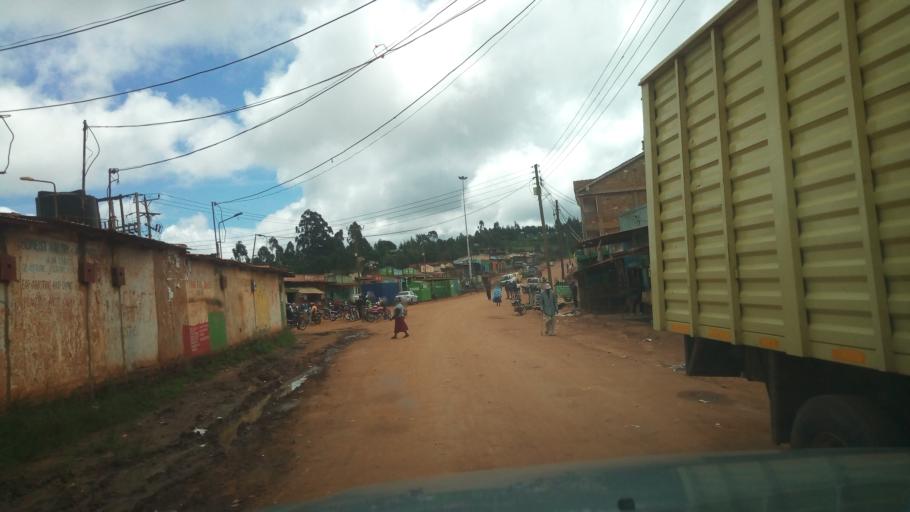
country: KE
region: Makueni
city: Wote
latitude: -1.6622
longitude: 37.4471
